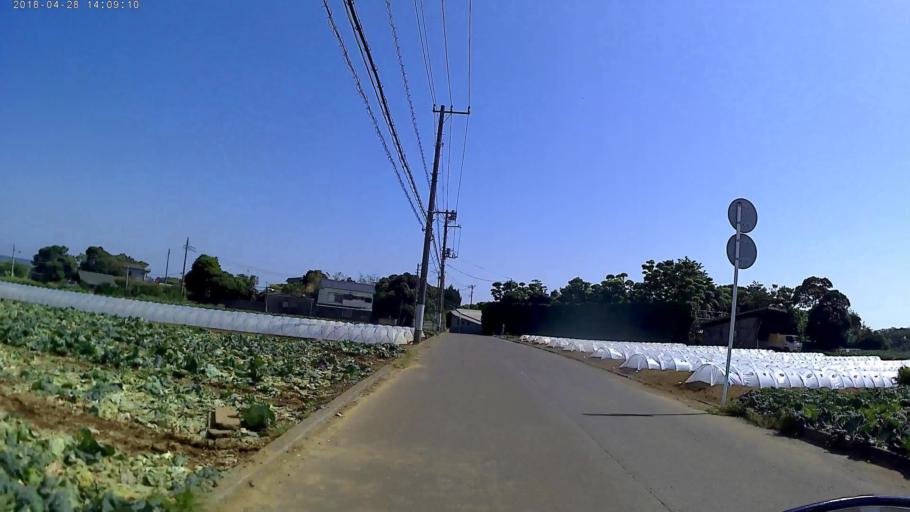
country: JP
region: Kanagawa
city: Miura
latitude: 35.1477
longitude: 139.6515
